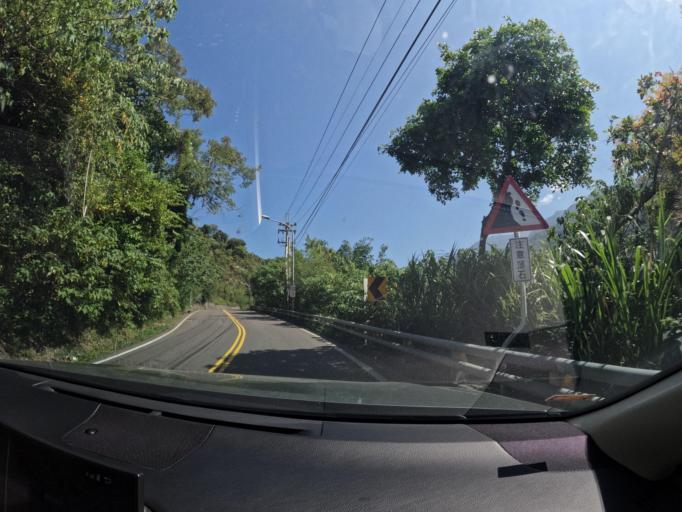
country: TW
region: Taiwan
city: Yujing
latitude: 23.1470
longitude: 120.7550
